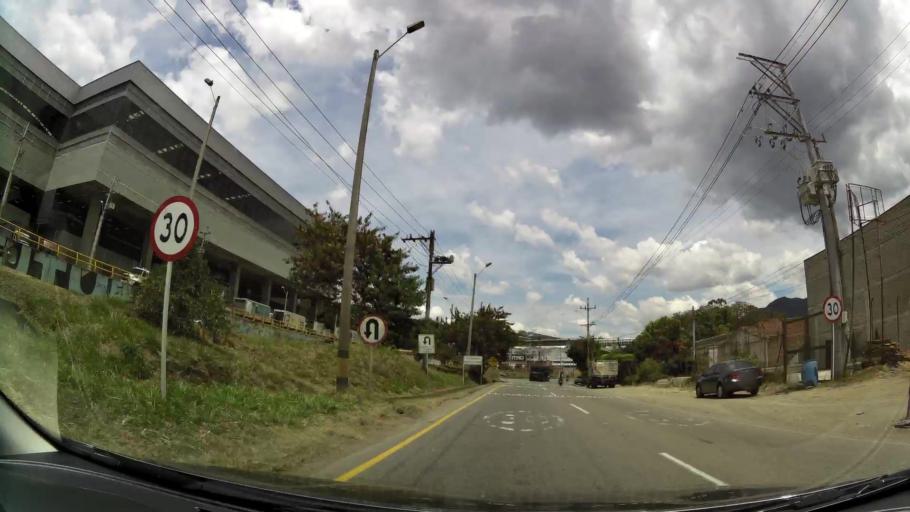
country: CO
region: Antioquia
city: Municipio de Copacabana
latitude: 6.3485
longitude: -75.5190
